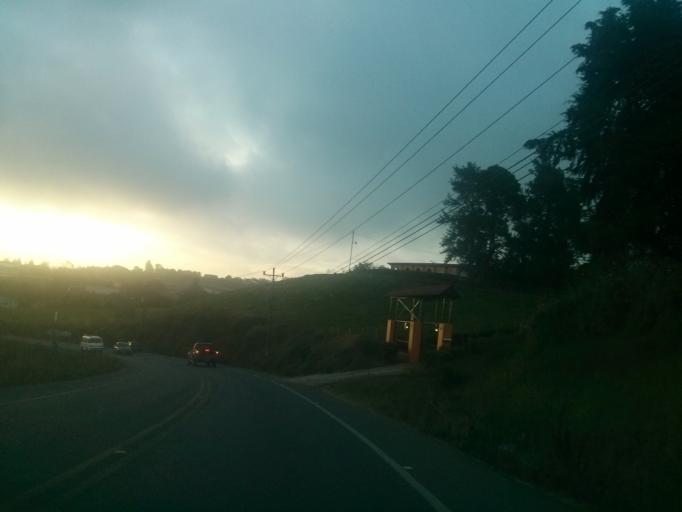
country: CR
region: Cartago
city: Cot
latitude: 9.8897
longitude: -83.8837
